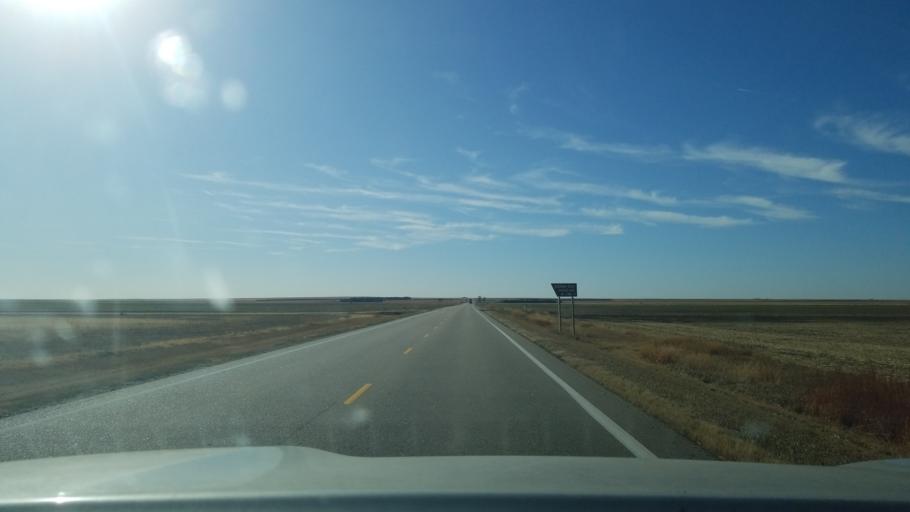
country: US
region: Kansas
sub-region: Ness County
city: Ness City
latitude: 38.3794
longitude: -99.8980
